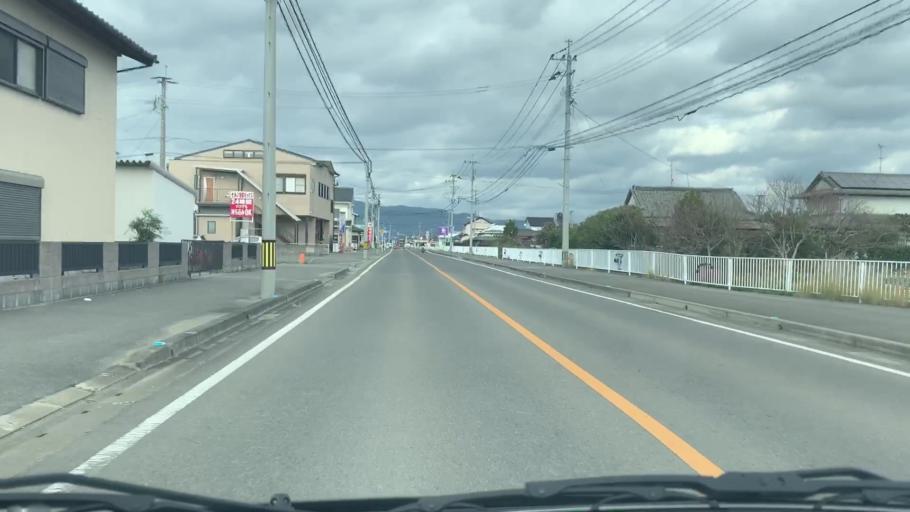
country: JP
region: Saga Prefecture
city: Saga-shi
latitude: 33.2458
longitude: 130.2379
